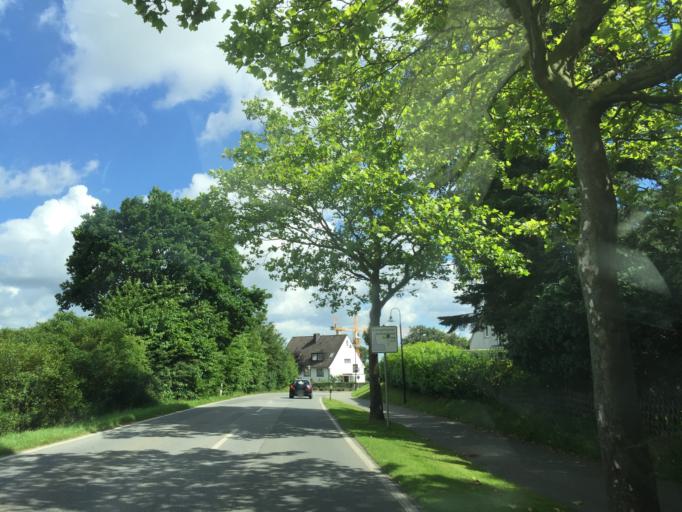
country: DE
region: Schleswig-Holstein
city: Scharbeutz
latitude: 54.0181
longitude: 10.7398
